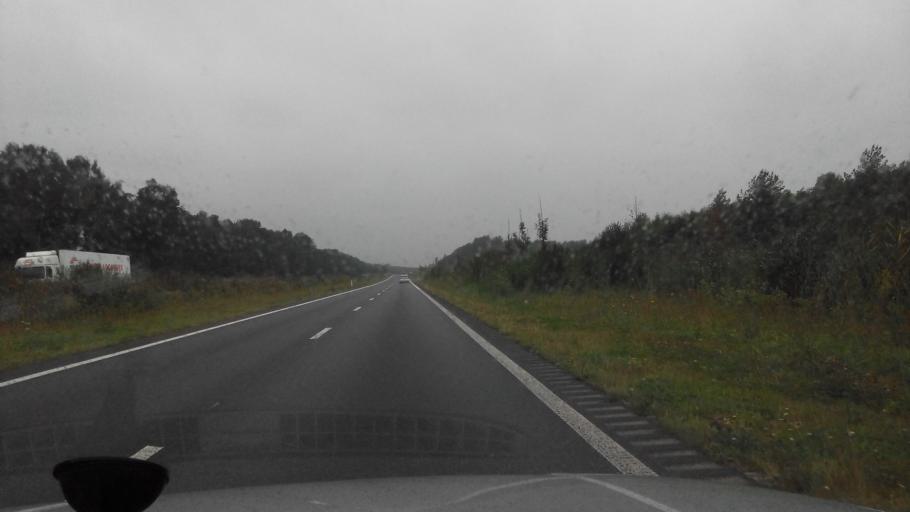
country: NL
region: Flevoland
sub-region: Gemeente Zeewolde
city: Zeewolde
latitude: 52.3429
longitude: 5.4932
